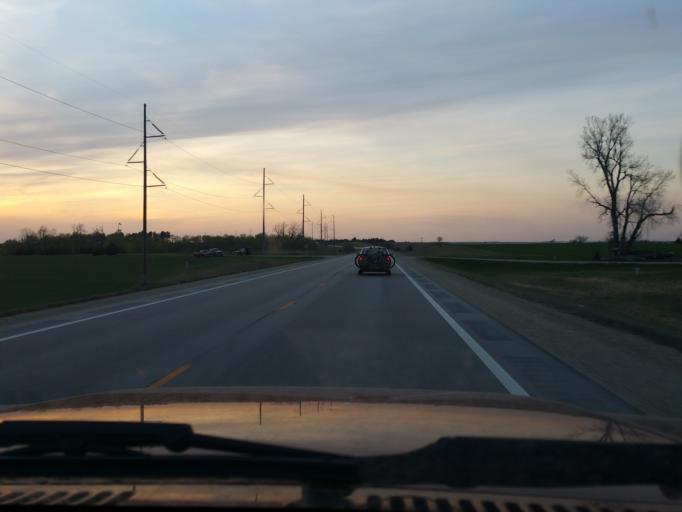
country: US
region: Kansas
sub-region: Riley County
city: Manhattan
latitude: 39.2679
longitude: -96.6867
